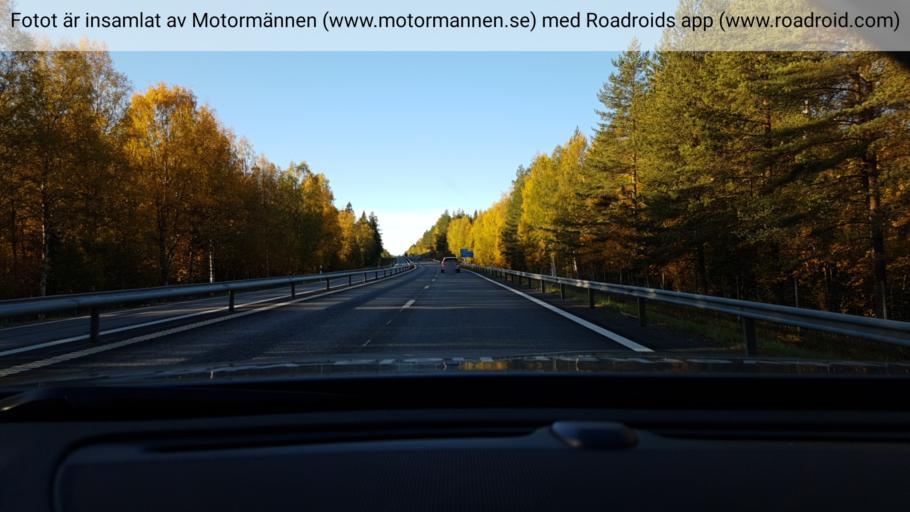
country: SE
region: Norrbotten
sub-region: Pitea Kommun
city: Norrfjarden
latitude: 65.3868
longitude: 21.4423
